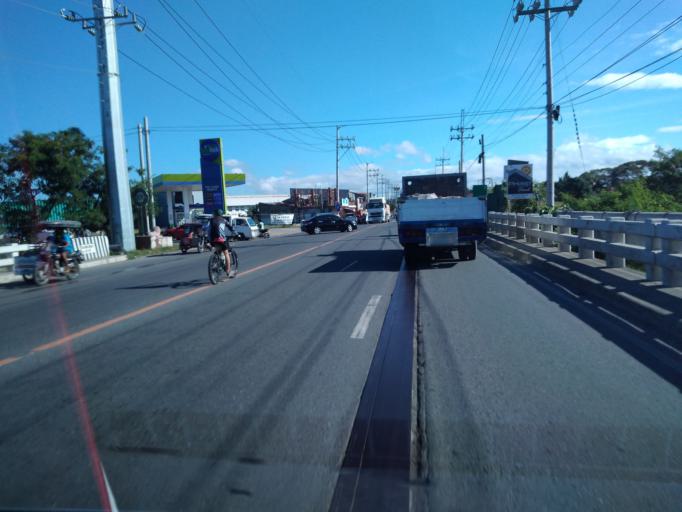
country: PH
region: Central Luzon
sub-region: Province of Bulacan
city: Santa Maria
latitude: 14.8184
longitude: 120.9499
